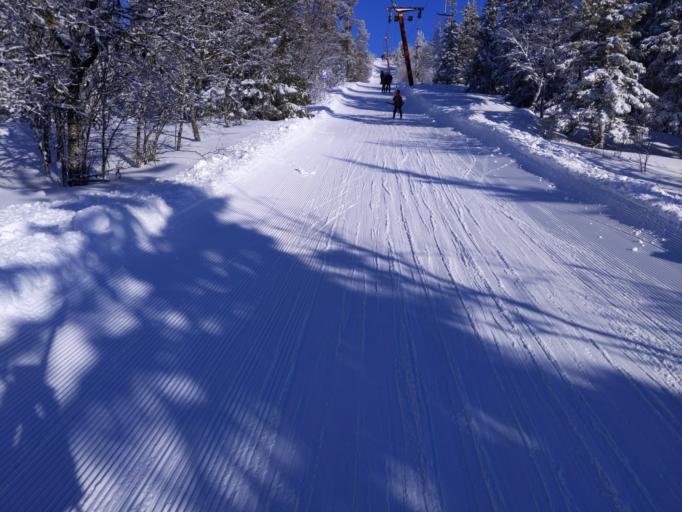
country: SE
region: Jaemtland
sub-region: Harjedalens Kommun
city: Sveg
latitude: 62.4308
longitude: 13.9596
